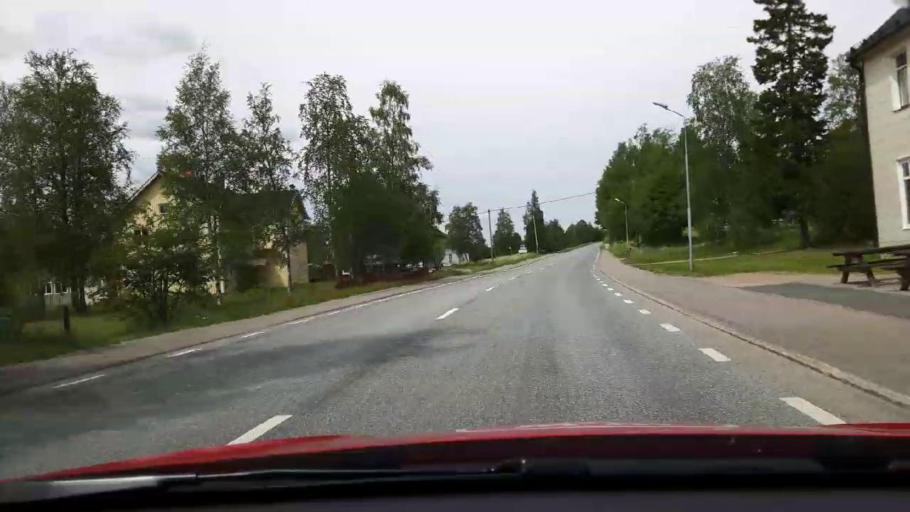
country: SE
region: Jaemtland
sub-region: Harjedalens Kommun
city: Sveg
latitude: 62.1575
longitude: 13.8894
